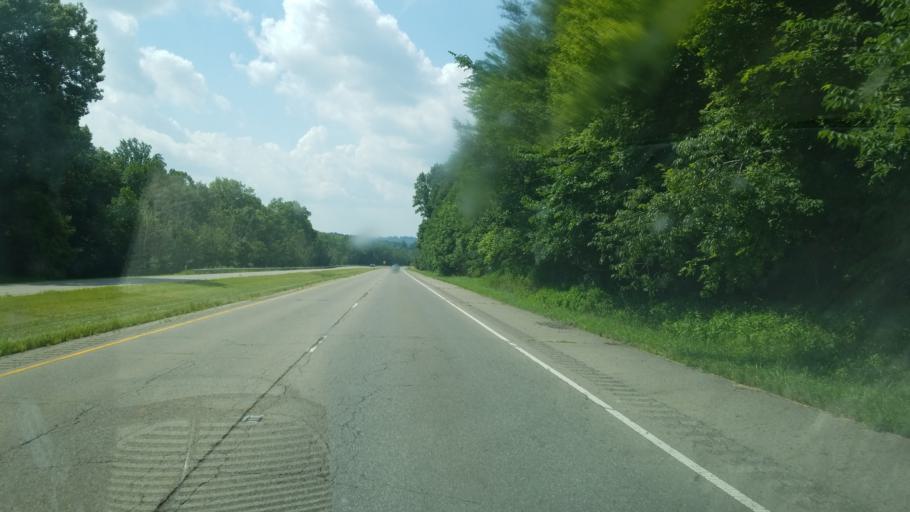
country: US
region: Ohio
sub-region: Richland County
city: Mansfield
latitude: 40.7169
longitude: -82.5031
